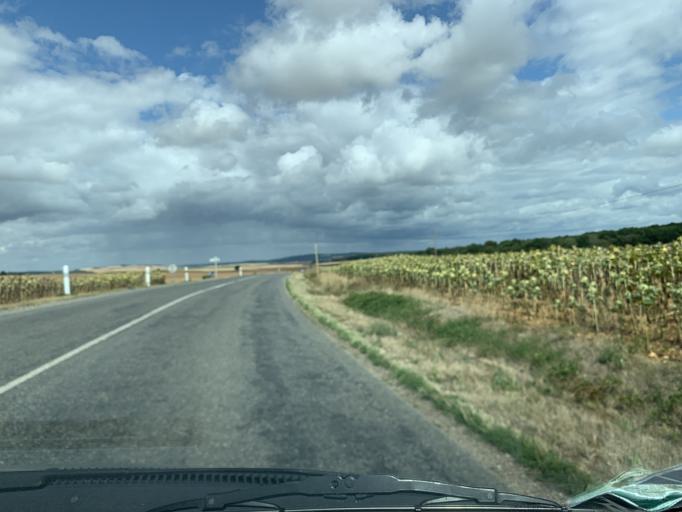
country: FR
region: Bourgogne
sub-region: Departement de la Nievre
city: Clamecy
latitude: 47.4118
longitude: 3.4548
